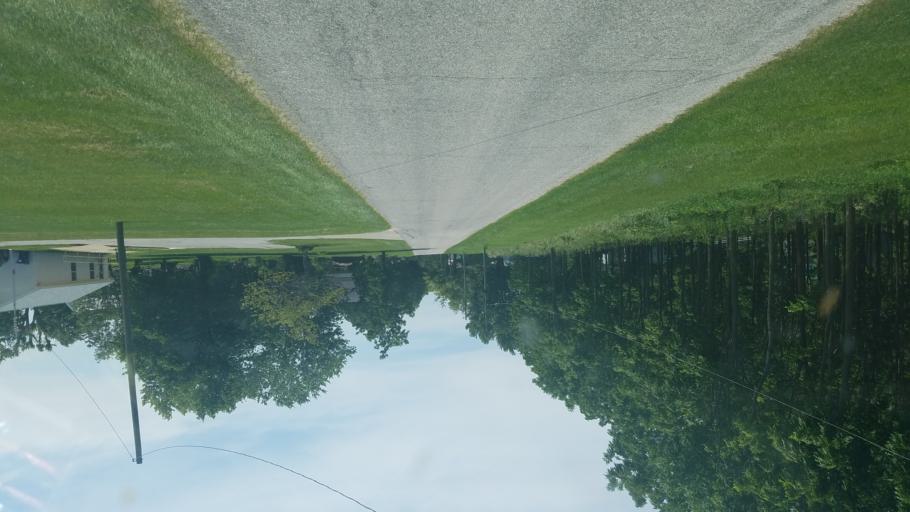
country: US
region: Ohio
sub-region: Crawford County
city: Bucyrus
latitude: 40.8710
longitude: -82.8803
